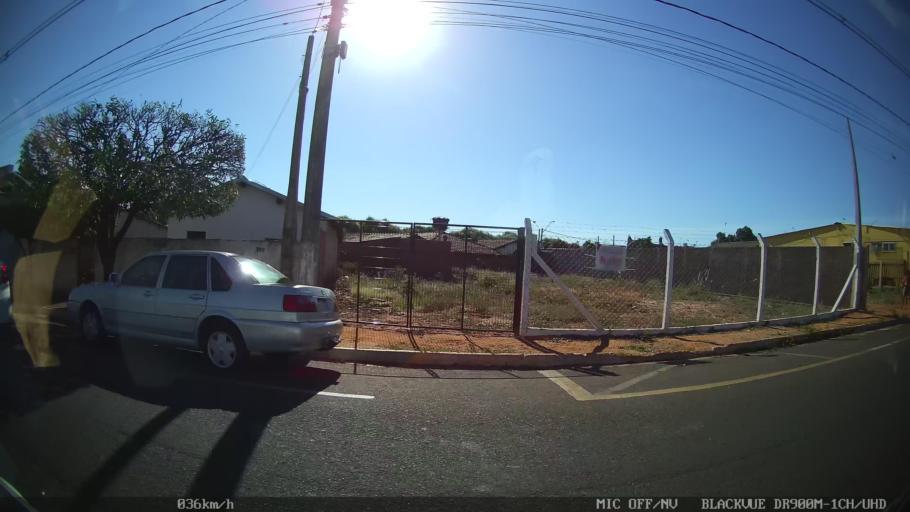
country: BR
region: Sao Paulo
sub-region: Olimpia
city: Olimpia
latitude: -20.7257
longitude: -48.9113
